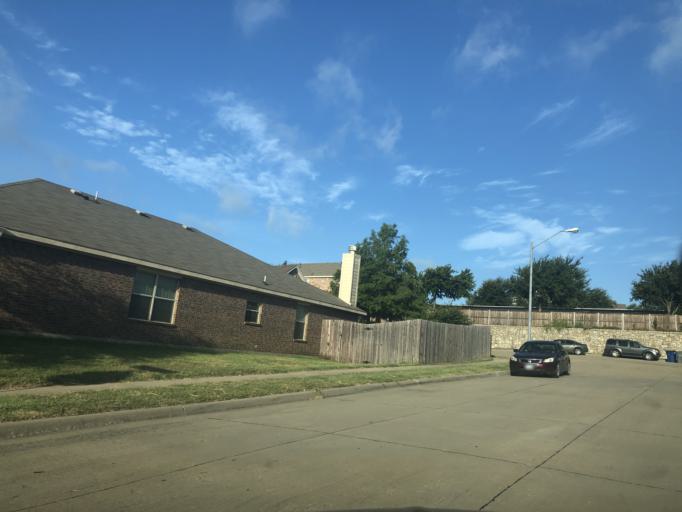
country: US
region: Texas
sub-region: Dallas County
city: Duncanville
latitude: 32.6655
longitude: -96.9403
